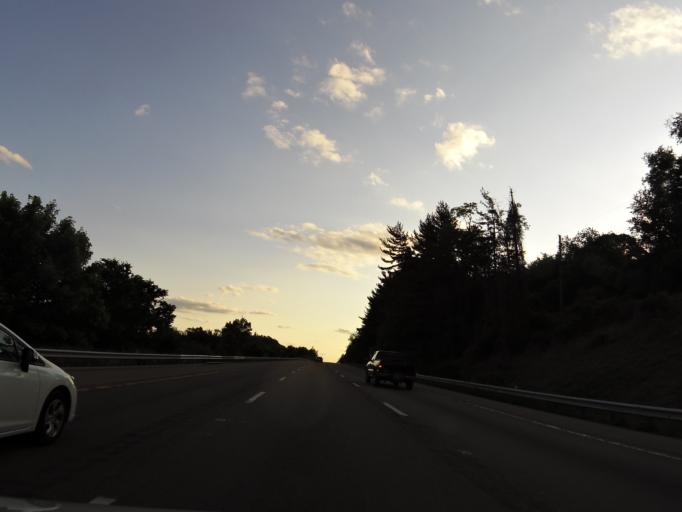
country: US
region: Virginia
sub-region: City of Bristol
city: Bristol
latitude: 36.6151
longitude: -82.2014
